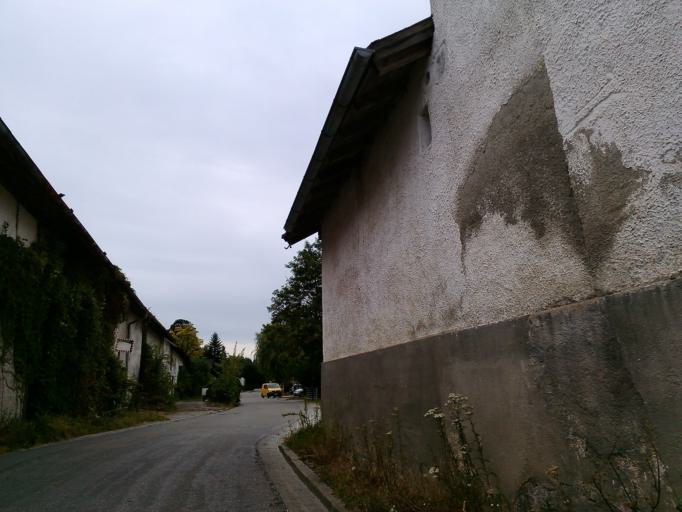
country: DE
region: Bavaria
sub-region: Upper Bavaria
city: Gauting
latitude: 48.0799
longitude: 11.3435
